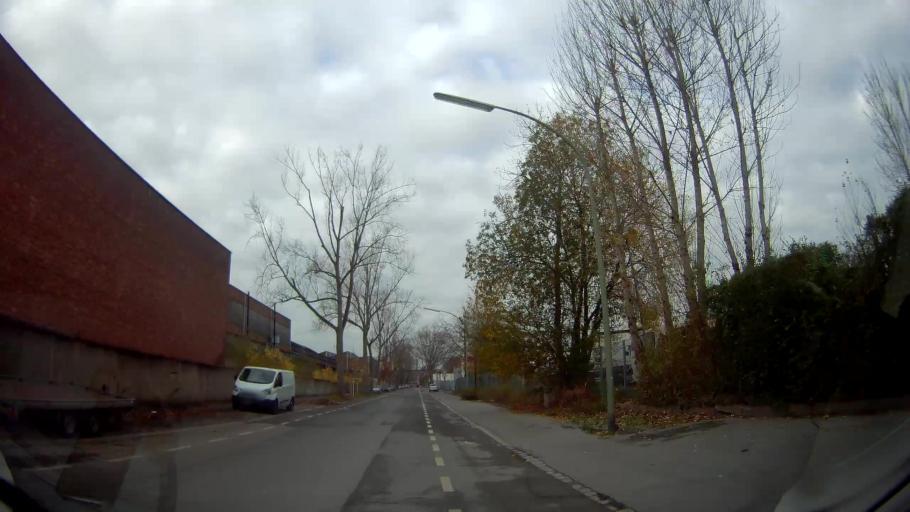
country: DE
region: North Rhine-Westphalia
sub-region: Regierungsbezirk Munster
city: Gelsenkirchen
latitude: 51.5283
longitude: 7.0913
